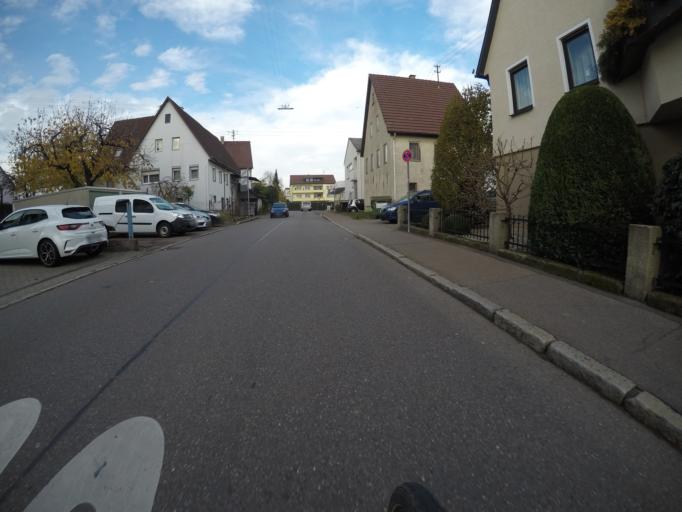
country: DE
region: Baden-Wuerttemberg
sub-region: Regierungsbezirk Stuttgart
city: Leinfelden-Echterdingen
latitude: 48.6907
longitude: 9.1646
